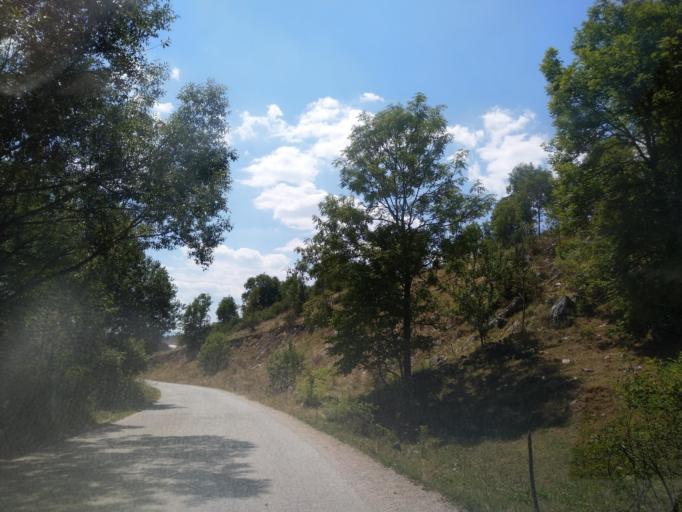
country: RS
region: Central Serbia
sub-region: Zlatiborski Okrug
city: Nova Varos
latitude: 43.4576
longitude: 19.9728
